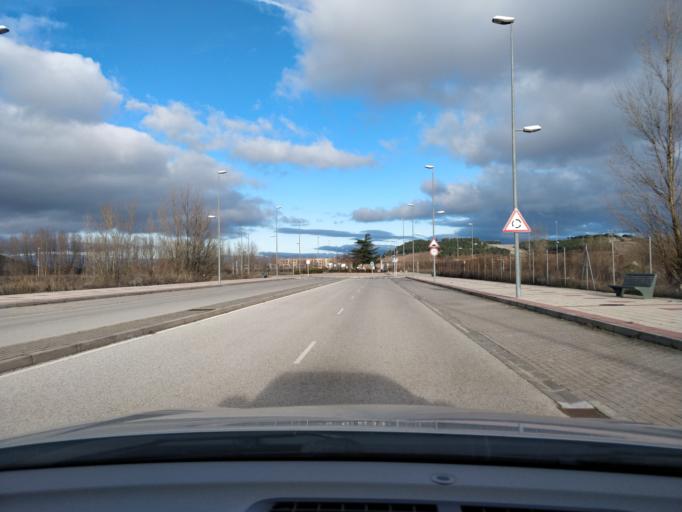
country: ES
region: Castille and Leon
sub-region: Provincia de Burgos
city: Villalbilla de Burgos
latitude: 42.3517
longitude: -3.7653
